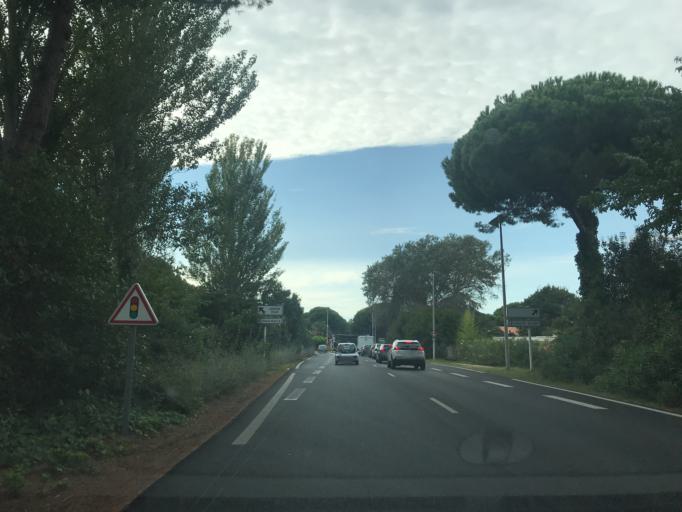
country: FR
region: Languedoc-Roussillon
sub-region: Departement de l'Herault
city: La Grande-Motte
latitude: 43.5636
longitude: 4.0879
